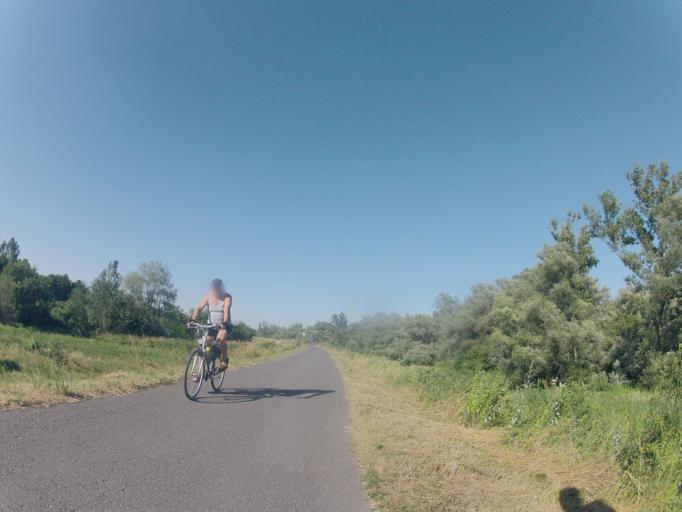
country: PL
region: Lesser Poland Voivodeship
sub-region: Krakow
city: Krakow
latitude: 50.0409
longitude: 19.8951
